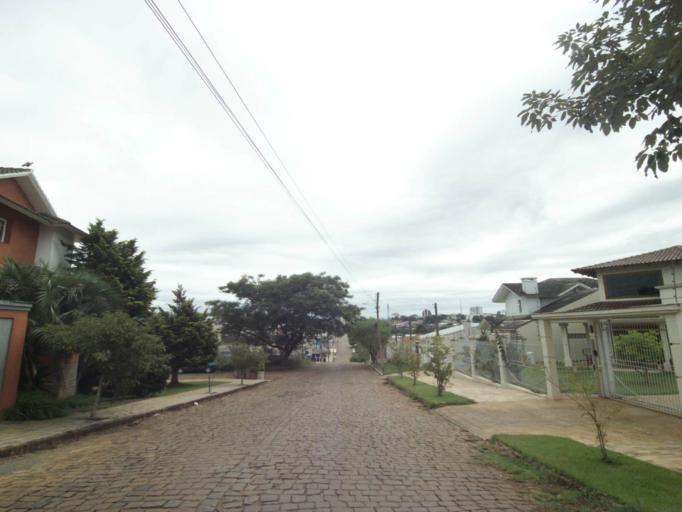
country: BR
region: Rio Grande do Sul
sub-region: Lagoa Vermelha
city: Lagoa Vermelha
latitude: -28.2171
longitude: -51.5322
